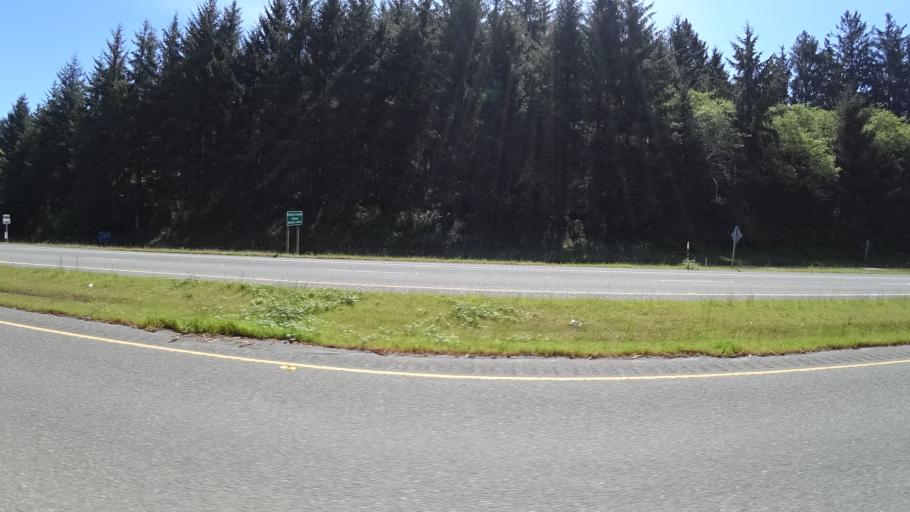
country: US
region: California
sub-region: Humboldt County
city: Westhaven-Moonstone
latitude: 41.1353
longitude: -124.1481
